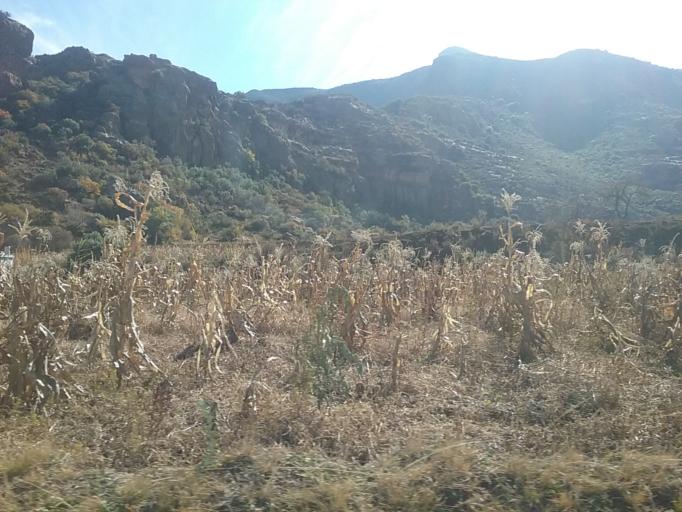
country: LS
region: Berea
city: Teyateyaneng
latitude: -29.2499
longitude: 27.9225
